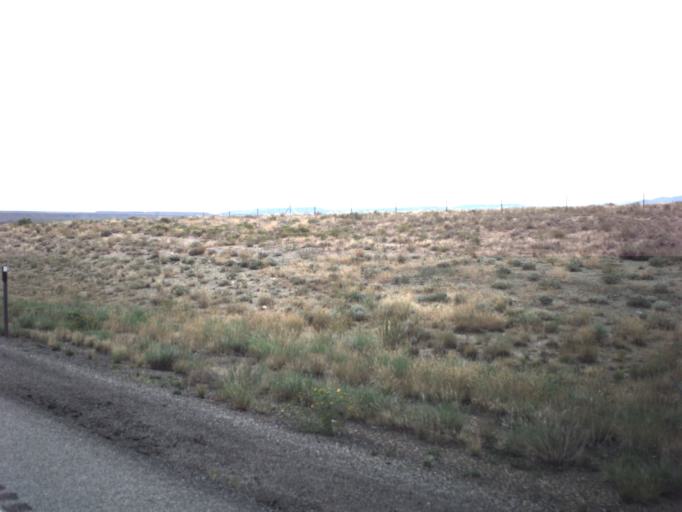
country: US
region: Utah
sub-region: Carbon County
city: Wellington
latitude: 39.5343
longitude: -110.5933
